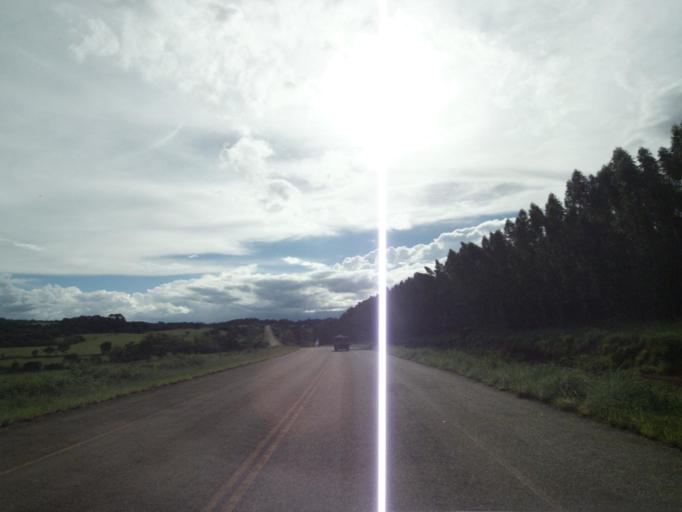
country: BR
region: Goias
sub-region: Jaragua
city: Jaragua
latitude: -15.8823
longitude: -49.4427
